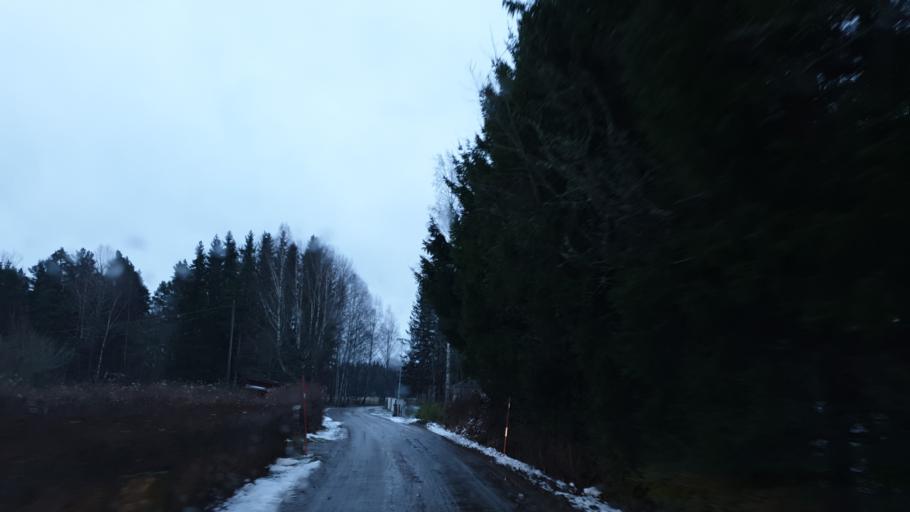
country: SE
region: Uppsala
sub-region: Tierps Kommun
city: Tierp
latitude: 60.3421
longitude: 17.4732
